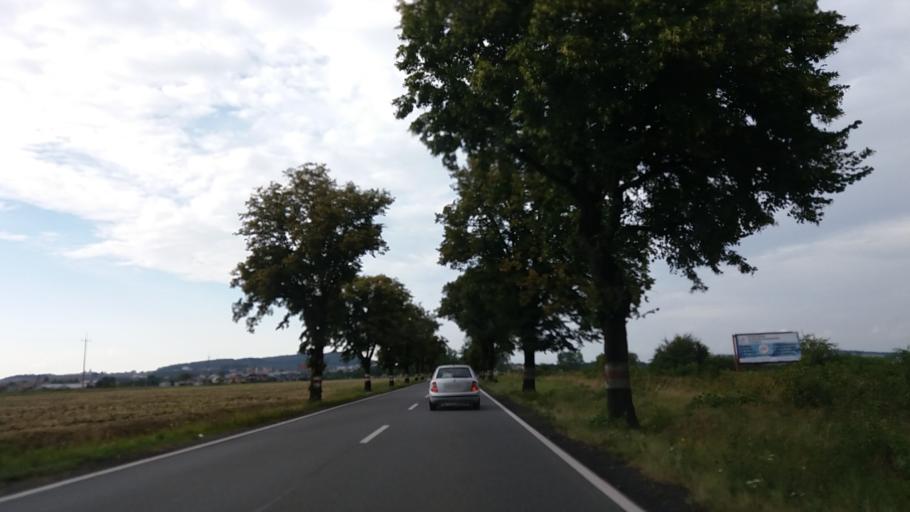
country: PL
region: Lower Silesian Voivodeship
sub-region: Powiat swidnicki
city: Stanowice
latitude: 50.9438
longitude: 16.3656
